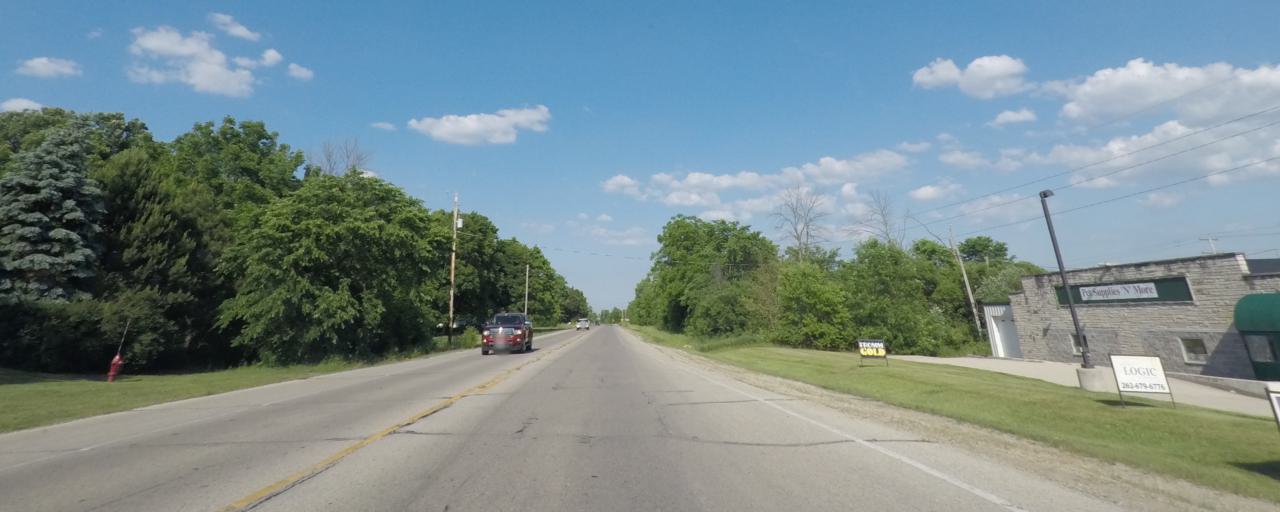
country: US
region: Wisconsin
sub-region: Waukesha County
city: Muskego
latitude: 42.8931
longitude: -88.1701
